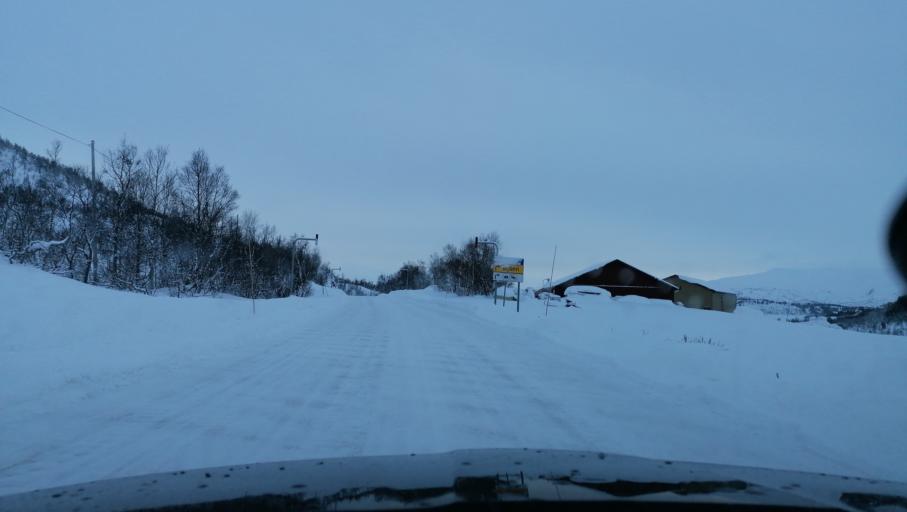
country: NO
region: Aust-Agder
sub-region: Bykle
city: Hovden
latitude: 59.6437
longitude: 7.4593
